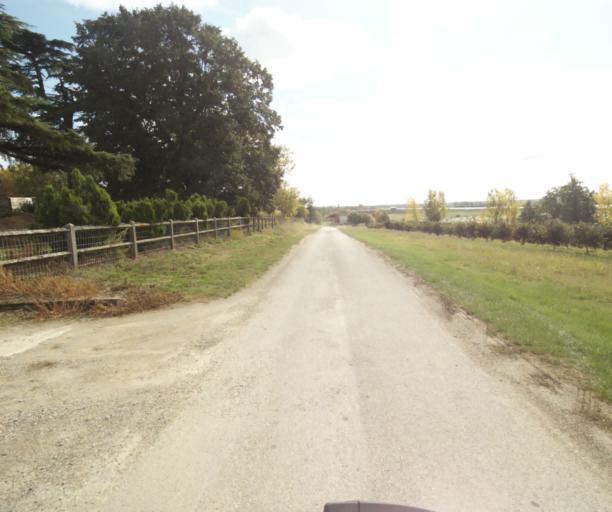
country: FR
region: Midi-Pyrenees
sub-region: Departement du Tarn-et-Garonne
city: Montech
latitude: 43.9495
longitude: 1.2075
